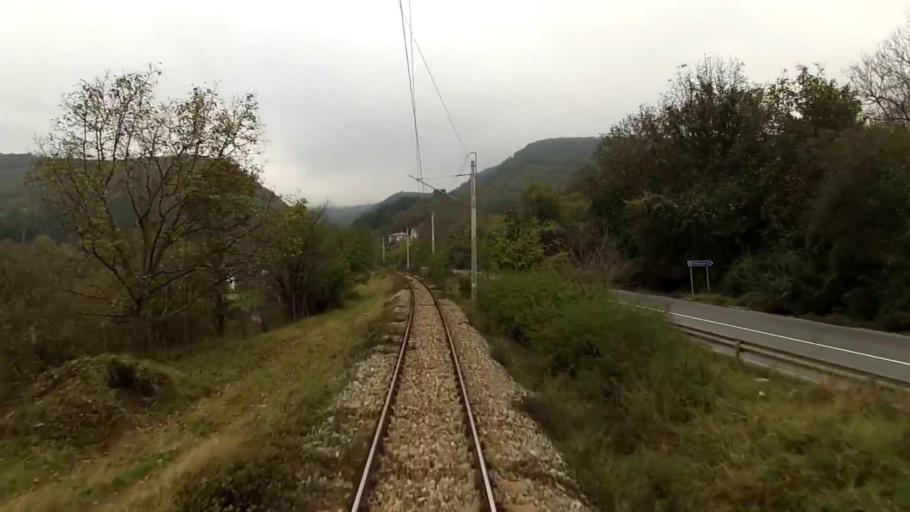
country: RS
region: Central Serbia
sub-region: Pirotski Okrug
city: Dimitrovgrad
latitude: 42.9787
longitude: 22.8497
